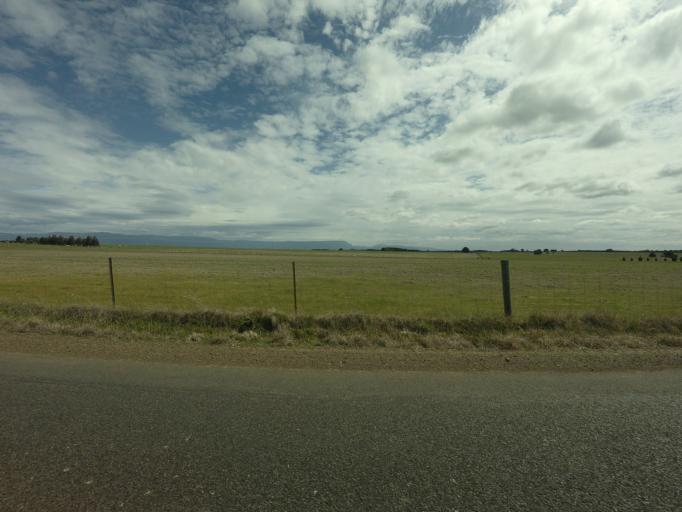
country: AU
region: Tasmania
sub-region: Northern Midlands
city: Longford
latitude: -41.7002
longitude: 147.1964
